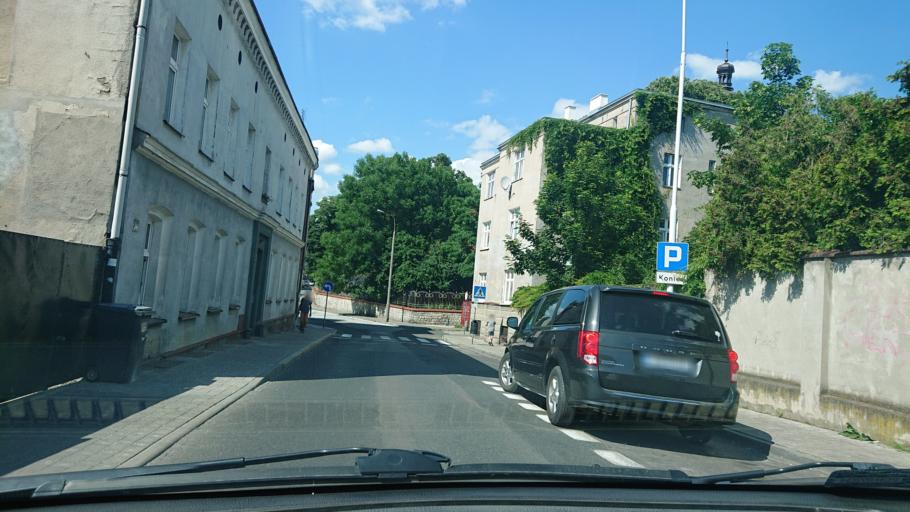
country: PL
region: Greater Poland Voivodeship
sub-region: Powiat gnieznienski
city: Gniezno
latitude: 52.5342
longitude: 17.5942
